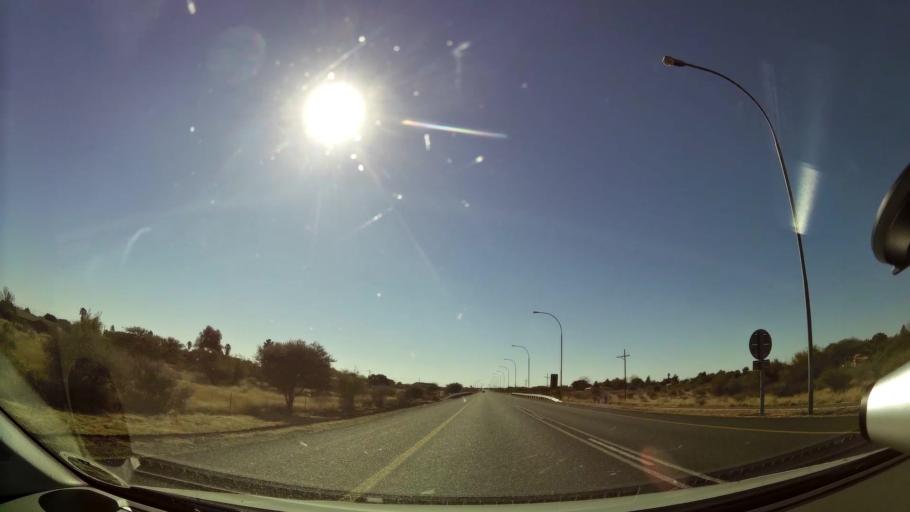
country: ZA
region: Northern Cape
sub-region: Frances Baard District Municipality
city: Warrenton
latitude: -28.1108
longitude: 24.8565
